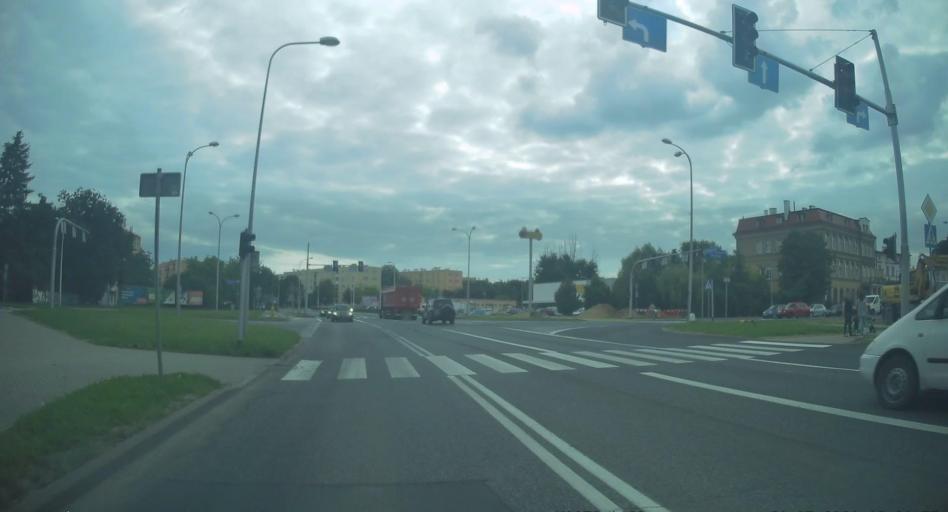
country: PL
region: Lower Silesian Voivodeship
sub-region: Powiat swidnicki
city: Swidnica
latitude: 50.8501
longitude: 16.4760
